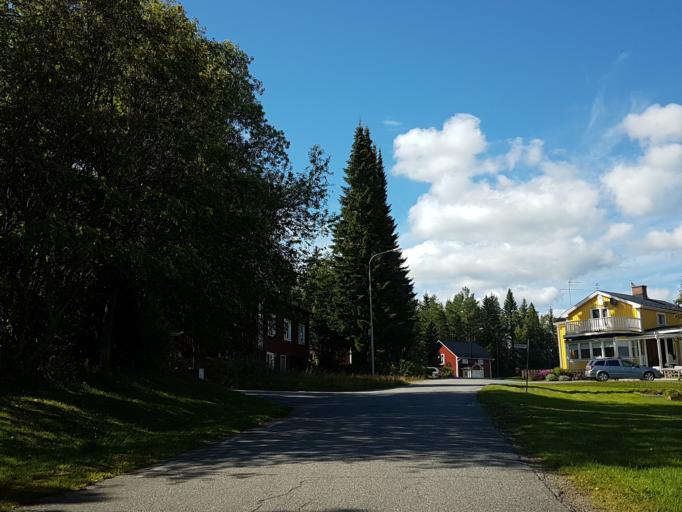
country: SE
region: Vaesterbotten
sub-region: Skelleftea Kommun
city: Burtraesk
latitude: 64.2685
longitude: 20.4933
